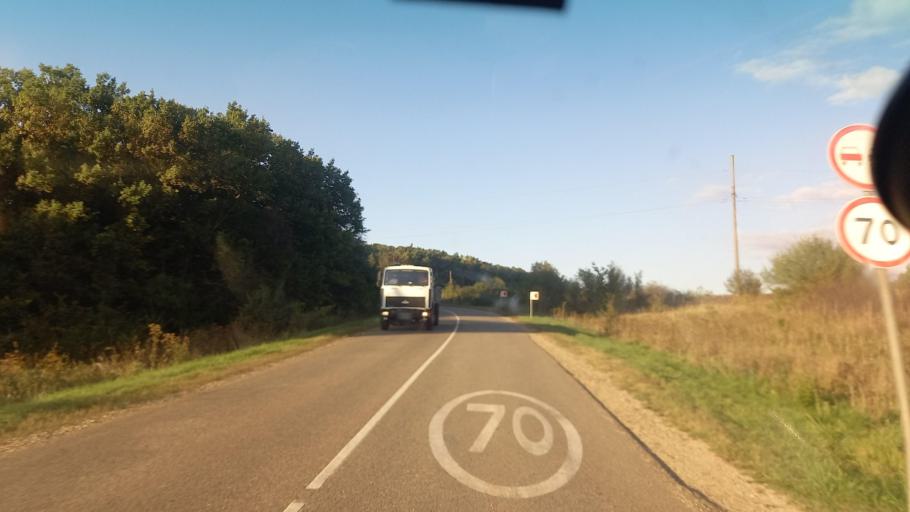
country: RU
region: Krasnodarskiy
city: Krymsk
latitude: 44.8968
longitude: 37.8991
